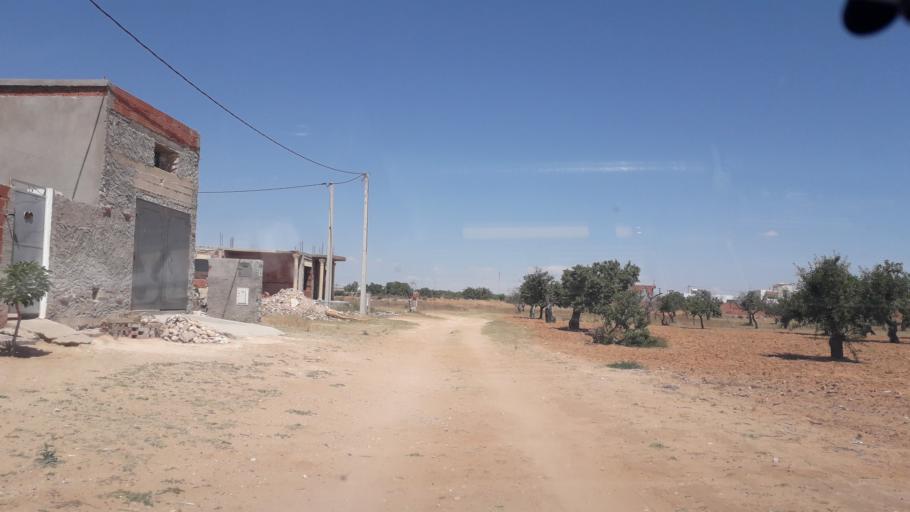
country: TN
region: Safaqis
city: Al Qarmadah
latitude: 34.8361
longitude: 10.7724
